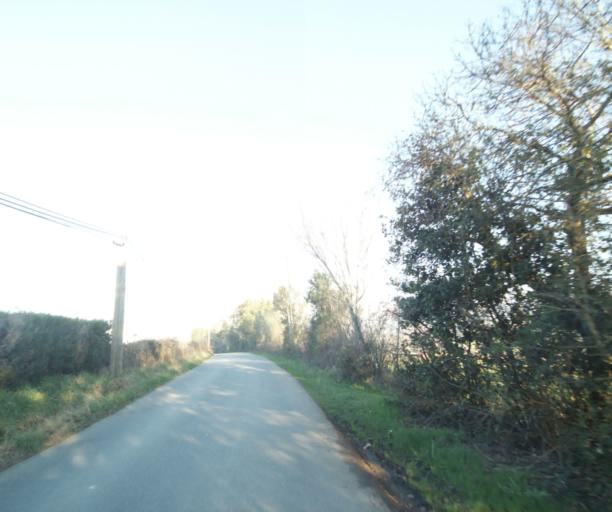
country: FR
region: Aquitaine
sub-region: Departement des Pyrenees-Atlantiques
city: Urrugne
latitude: 43.3426
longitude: -1.7011
